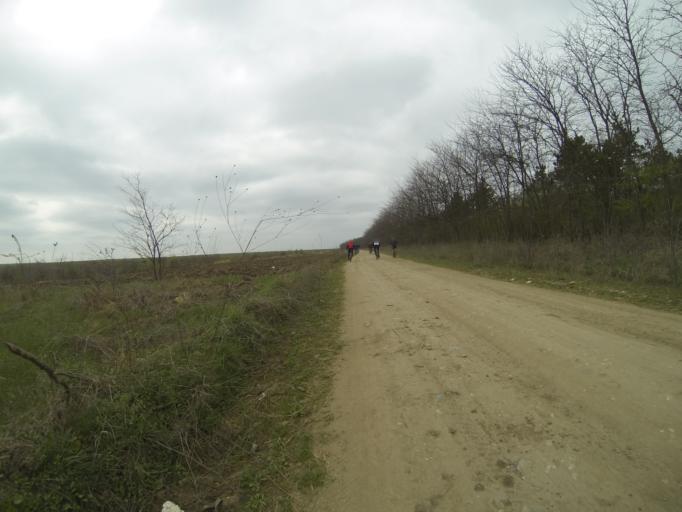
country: RO
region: Dolj
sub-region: Comuna Predesti
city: Predesti
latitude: 44.3399
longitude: 23.6370
